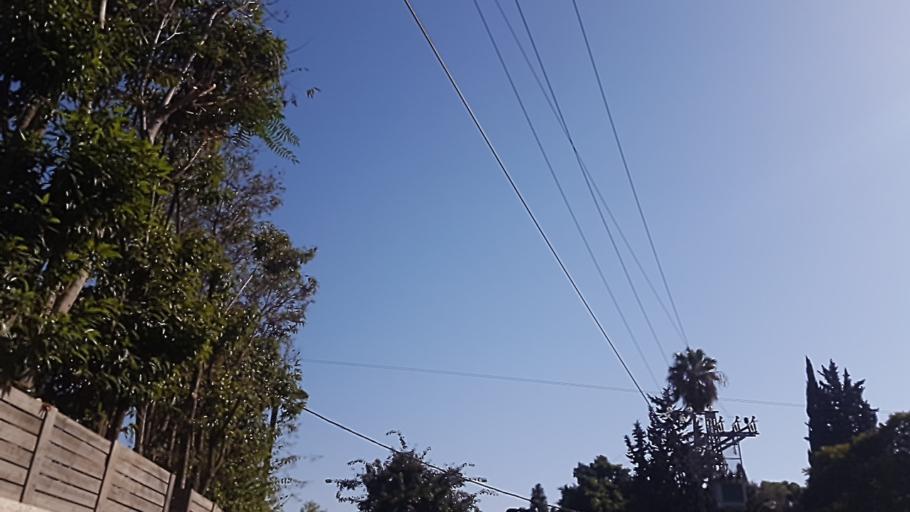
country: IL
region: Tel Aviv
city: Giv`atayim
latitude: 32.0592
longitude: 34.8213
